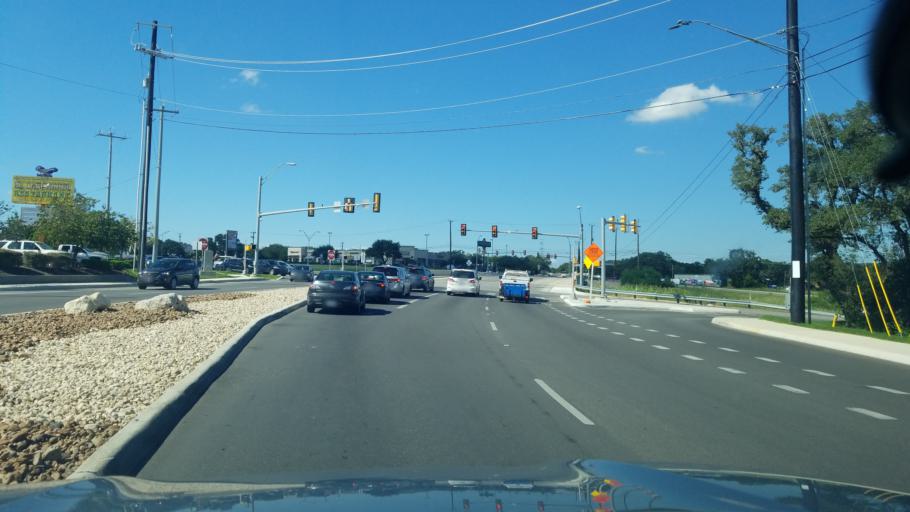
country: US
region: Texas
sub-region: Bexar County
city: Hollywood Park
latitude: 29.6014
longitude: -98.4428
